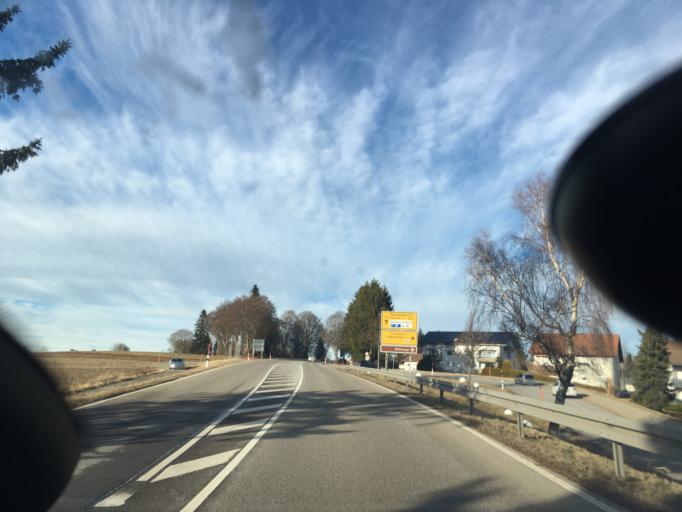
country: DE
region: Baden-Wuerttemberg
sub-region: Freiburg Region
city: Hochenschwand
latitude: 47.7301
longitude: 8.1625
